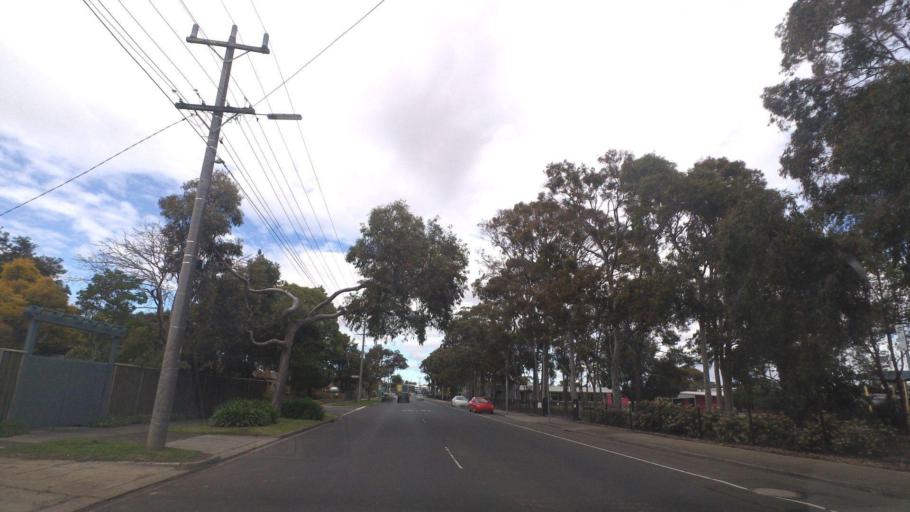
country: AU
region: Victoria
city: Macleod
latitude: -37.7274
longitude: 145.0610
